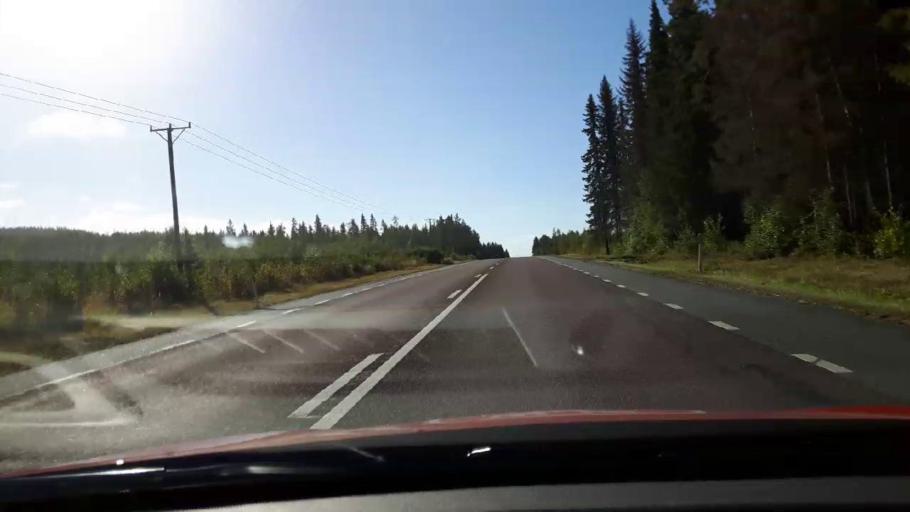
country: SE
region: Jaemtland
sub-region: Braecke Kommun
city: Braecke
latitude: 62.8660
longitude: 15.3093
